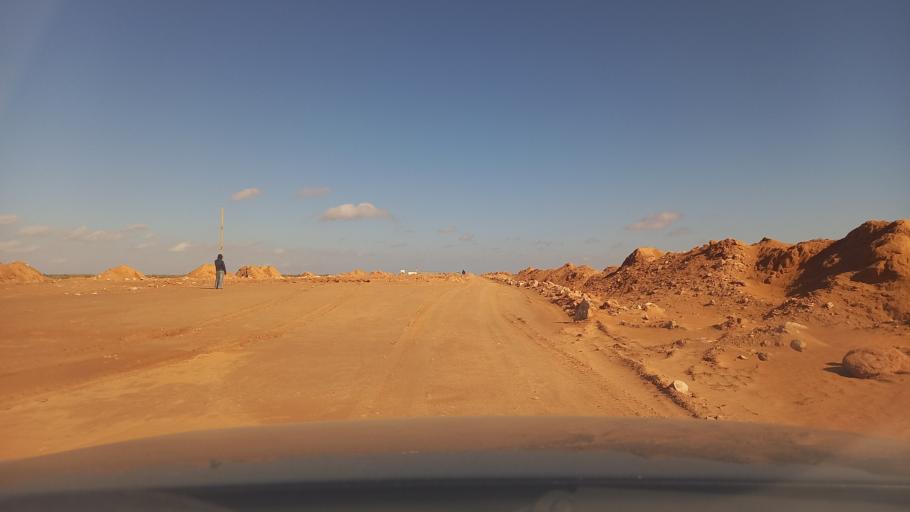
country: TN
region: Madanin
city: Medenine
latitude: 33.2458
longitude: 10.5607
